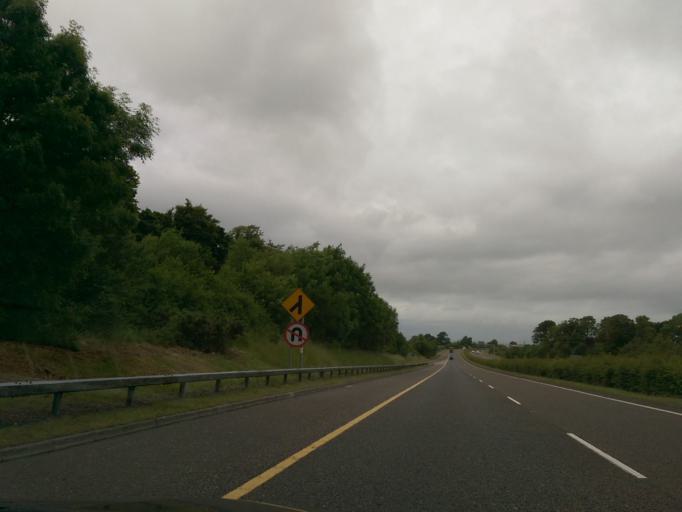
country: IE
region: Munster
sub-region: An Clar
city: Newmarket on Fergus
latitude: 52.7527
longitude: -8.9043
